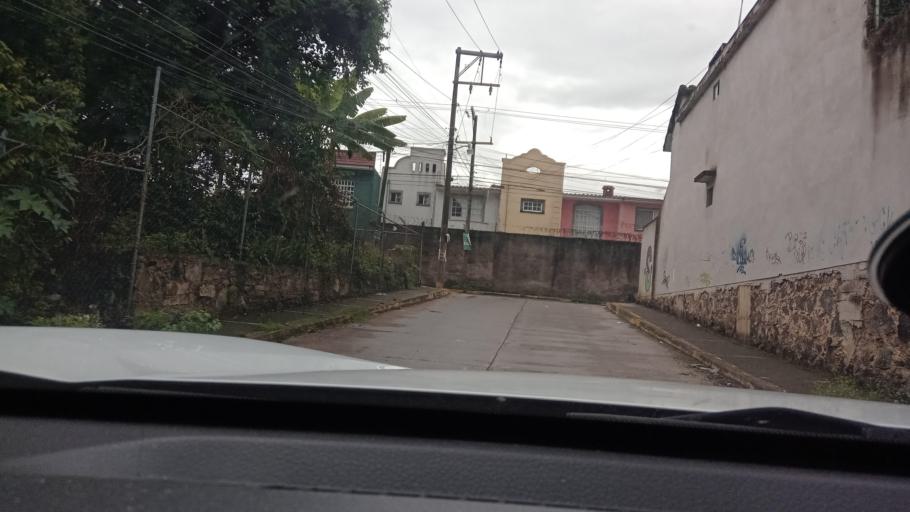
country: MX
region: Veracruz
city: Coatepec
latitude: 19.4452
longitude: -96.9697
